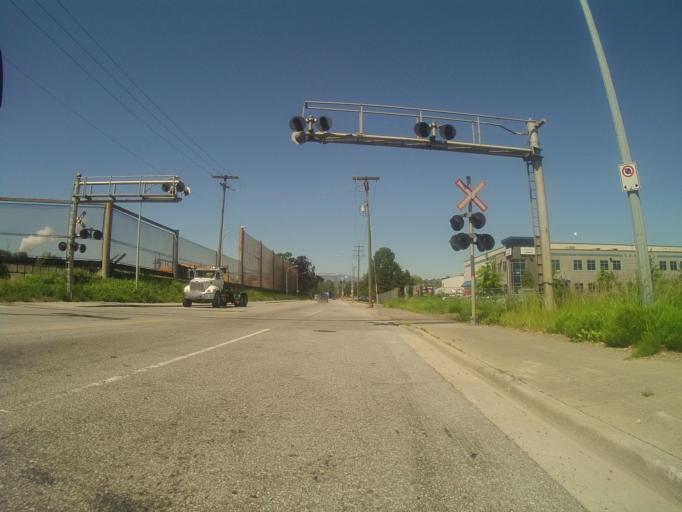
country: CA
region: British Columbia
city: Vancouver
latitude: 49.1989
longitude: -123.0691
